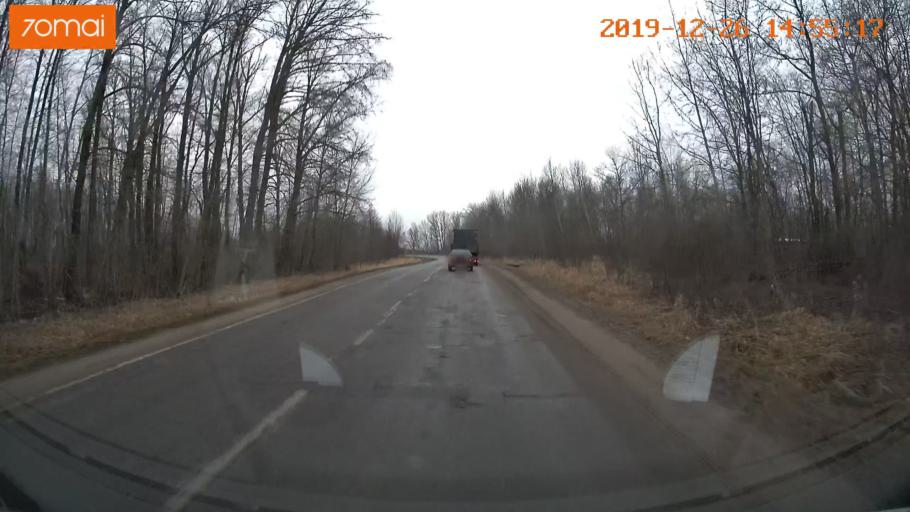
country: RU
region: Jaroslavl
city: Rybinsk
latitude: 58.3018
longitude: 38.8767
